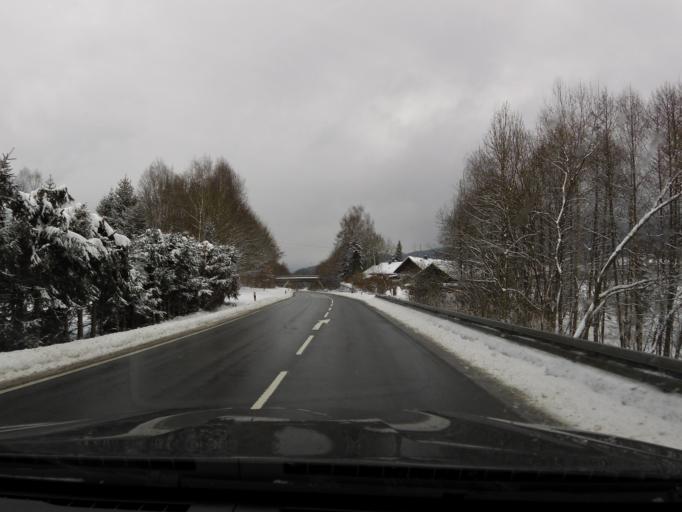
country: DE
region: Bavaria
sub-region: Lower Bavaria
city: Lalling
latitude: 48.8229
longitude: 13.1387
